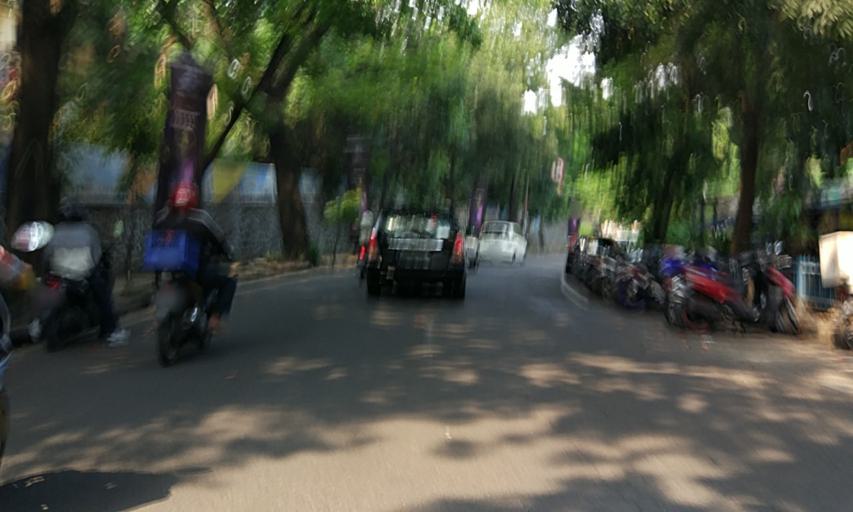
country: ID
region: West Java
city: Bandung
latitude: -6.9047
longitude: 107.6081
